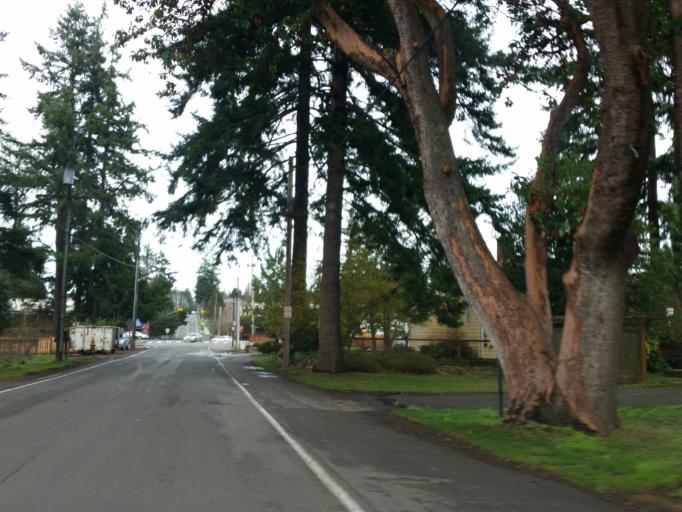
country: US
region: Washington
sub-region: Snohomish County
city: Woodway
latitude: 47.7695
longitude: -122.3826
